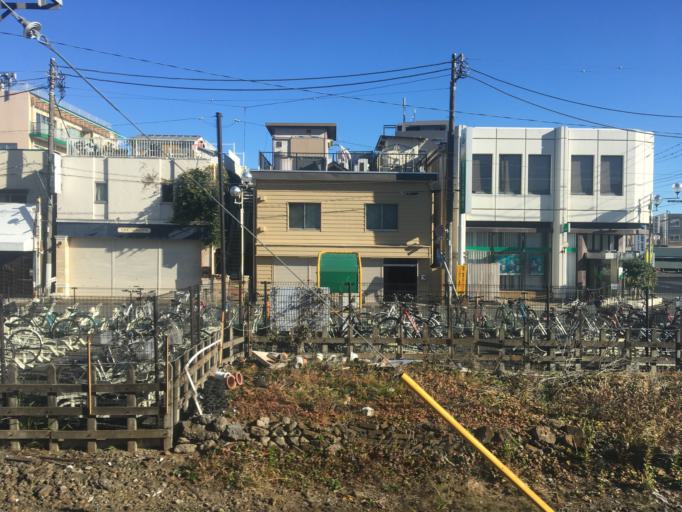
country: JP
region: Saitama
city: Sakado
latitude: 35.9373
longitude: 139.4232
